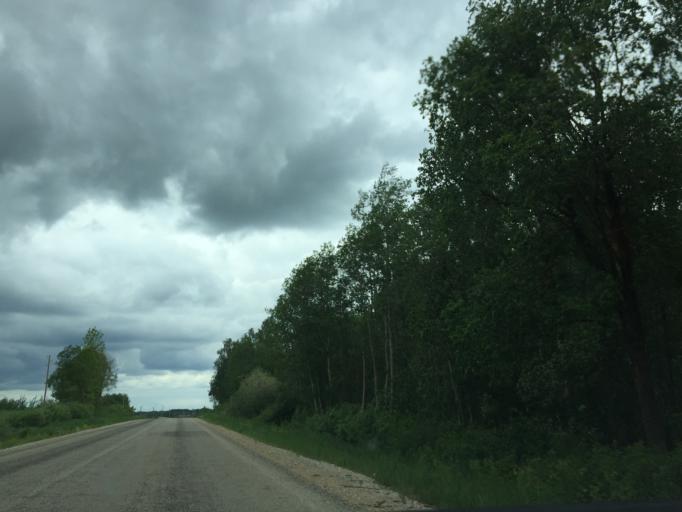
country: LV
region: Dagda
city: Dagda
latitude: 56.0706
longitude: 27.5546
